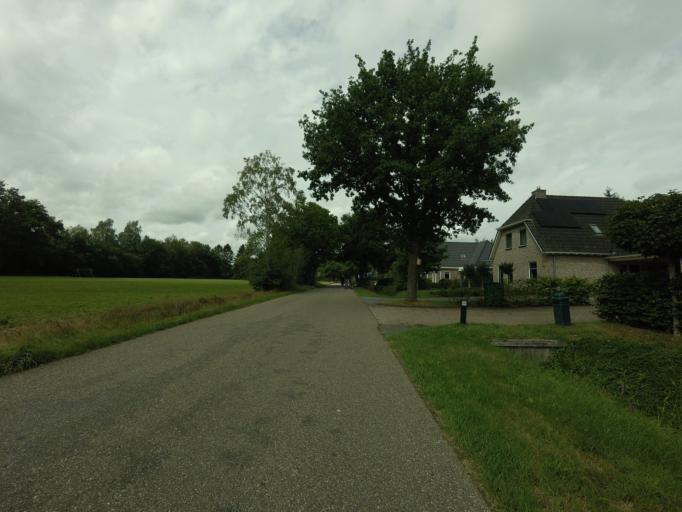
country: NL
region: Friesland
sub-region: Gemeente Heerenveen
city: Nieuwehorne
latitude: 52.9141
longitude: 6.0772
